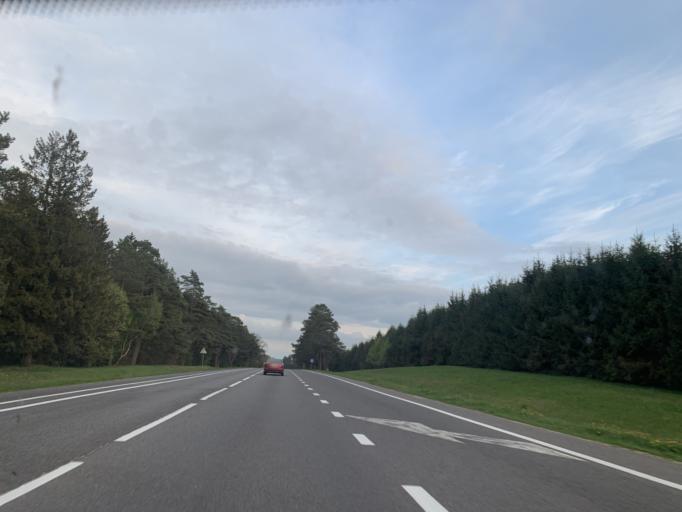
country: BY
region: Minsk
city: Haradzyeya
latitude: 53.2834
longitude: 26.5871
